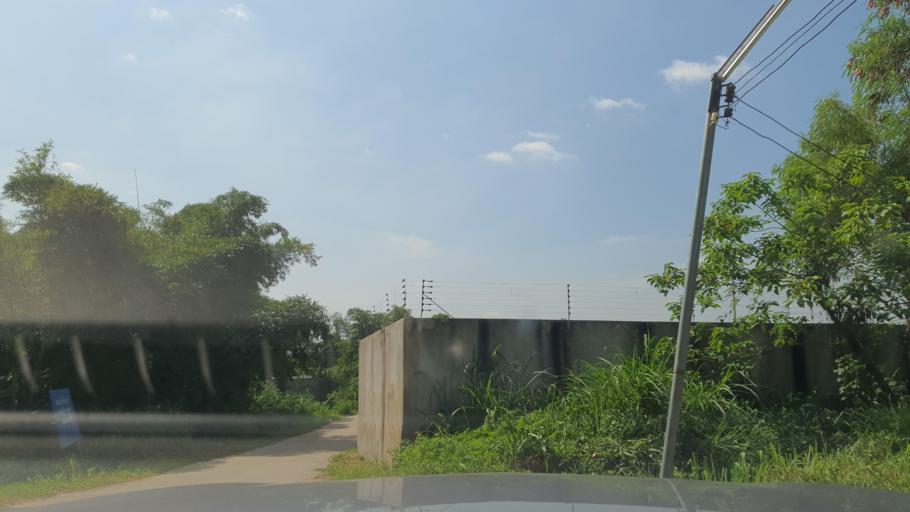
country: TH
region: Chiang Mai
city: Hang Dong
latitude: 18.7221
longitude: 98.9122
